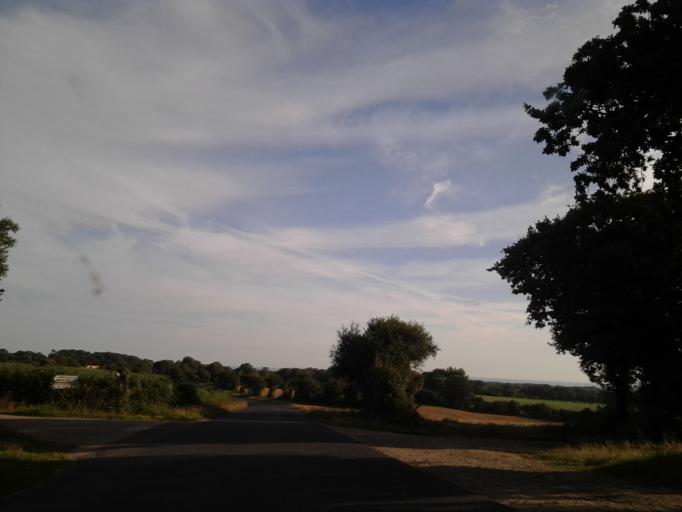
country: FR
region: Lower Normandy
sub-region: Departement de la Manche
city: Fermanville
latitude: 49.6483
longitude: -1.4426
